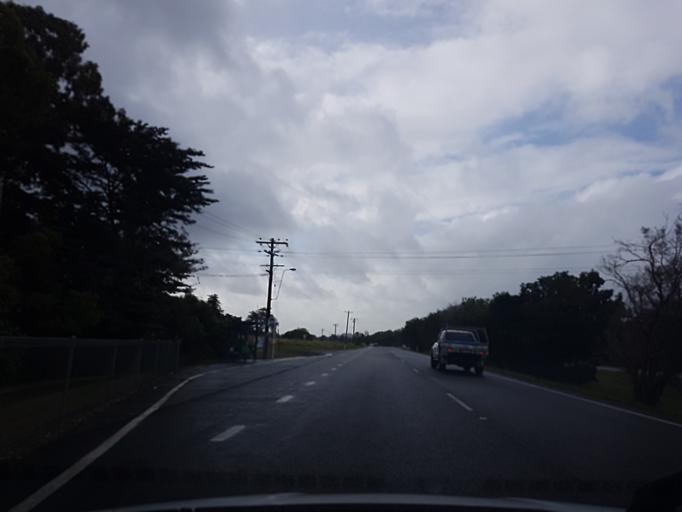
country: AU
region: Queensland
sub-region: Cairns
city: Trinity Beach
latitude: -16.8178
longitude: 145.6930
